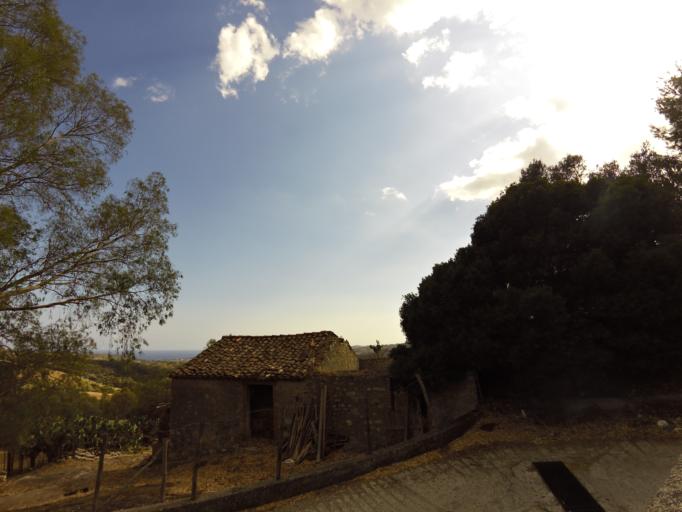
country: IT
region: Calabria
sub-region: Provincia di Reggio Calabria
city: Riace
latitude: 38.4103
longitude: 16.4843
